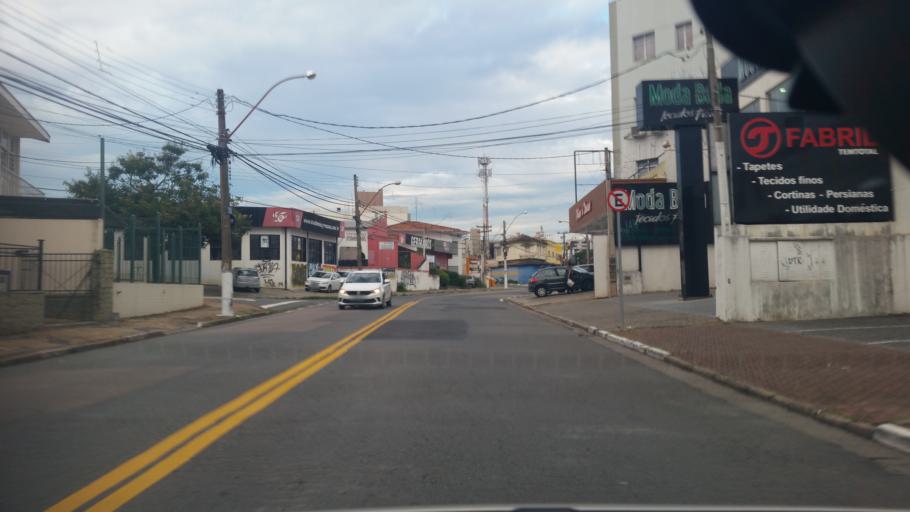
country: BR
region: Sao Paulo
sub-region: Campinas
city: Campinas
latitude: -22.8854
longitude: -47.0555
